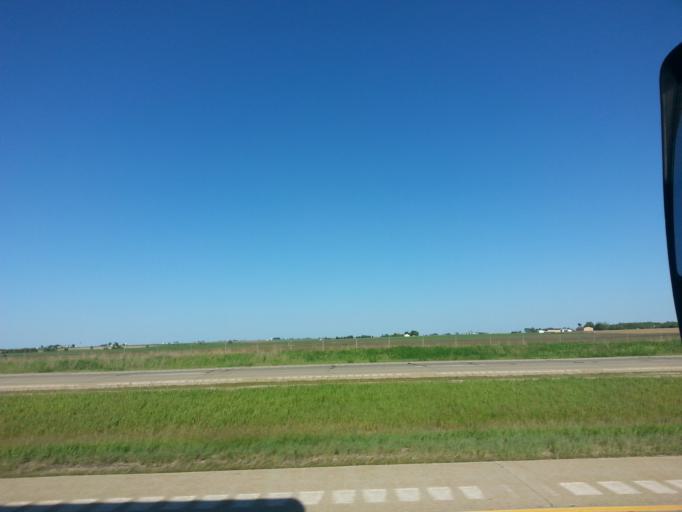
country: US
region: Illinois
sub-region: Marshall County
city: Wenona
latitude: 41.0672
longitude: -89.0673
